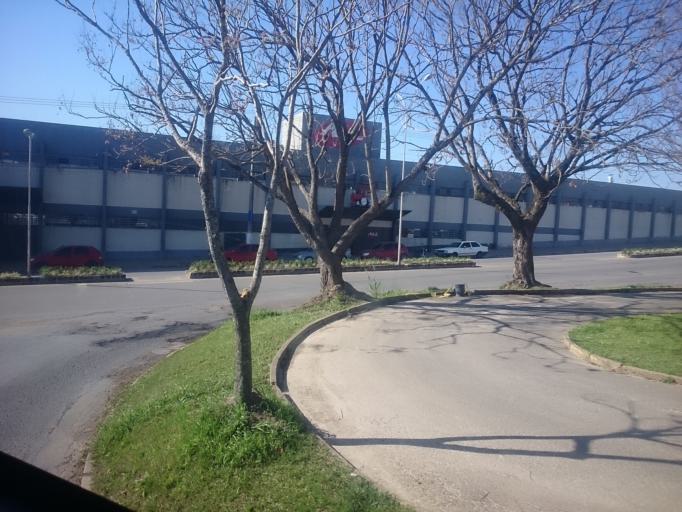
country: BR
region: Santa Catarina
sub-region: Mafra
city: Mafra
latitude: -26.1132
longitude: -49.8007
